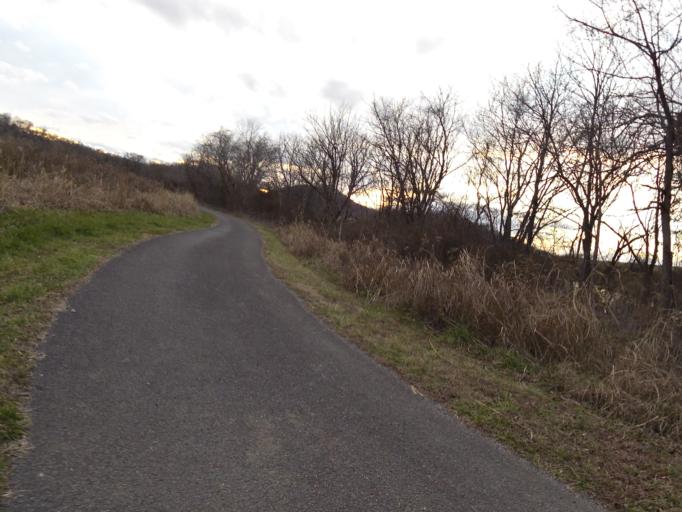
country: US
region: Tennessee
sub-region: Knox County
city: Knoxville
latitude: 35.9562
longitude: -83.8520
